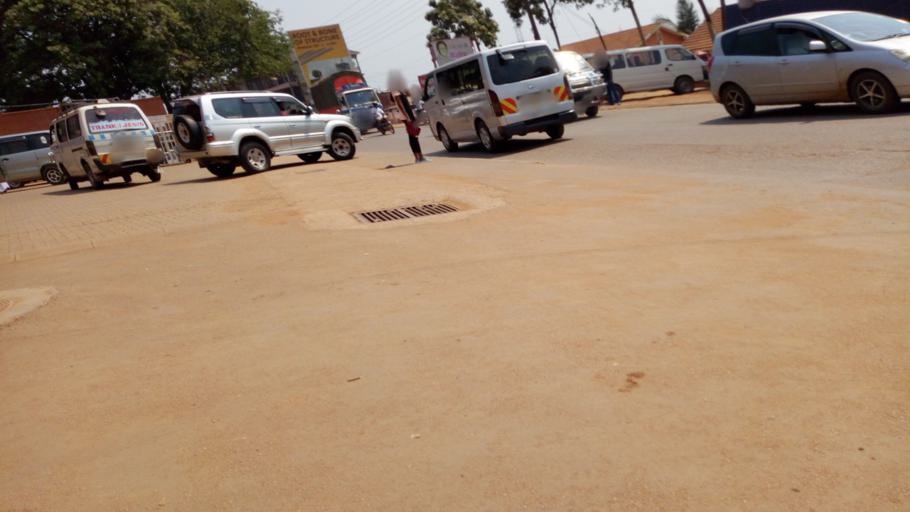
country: UG
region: Central Region
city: Kampala Central Division
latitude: 0.3466
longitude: 32.5672
